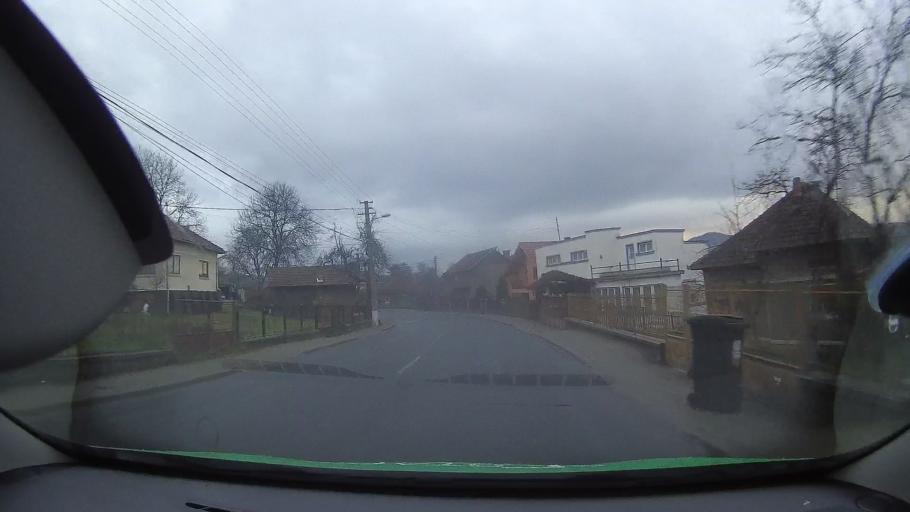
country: RO
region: Hunedoara
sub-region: Municipiul Brad
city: Brad
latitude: 46.1278
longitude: 22.7855
